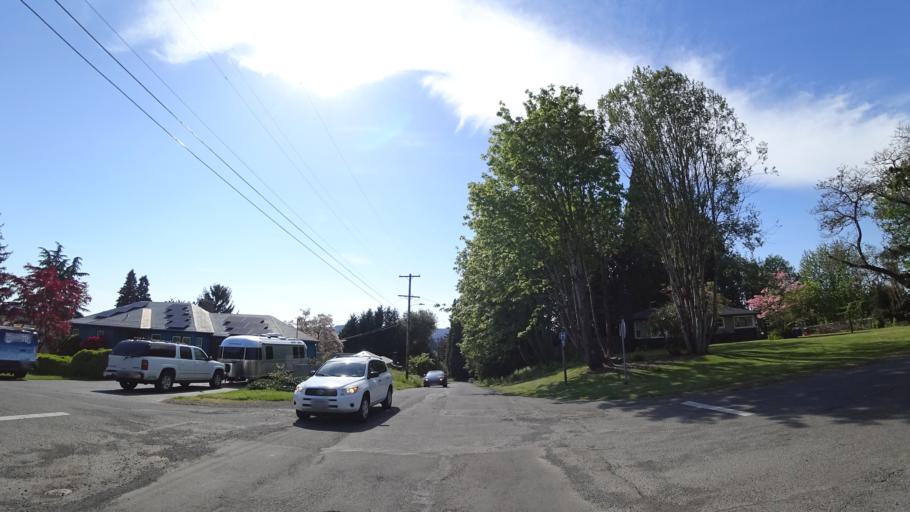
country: US
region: Oregon
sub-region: Clackamas County
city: Milwaukie
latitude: 45.4481
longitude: -122.6258
